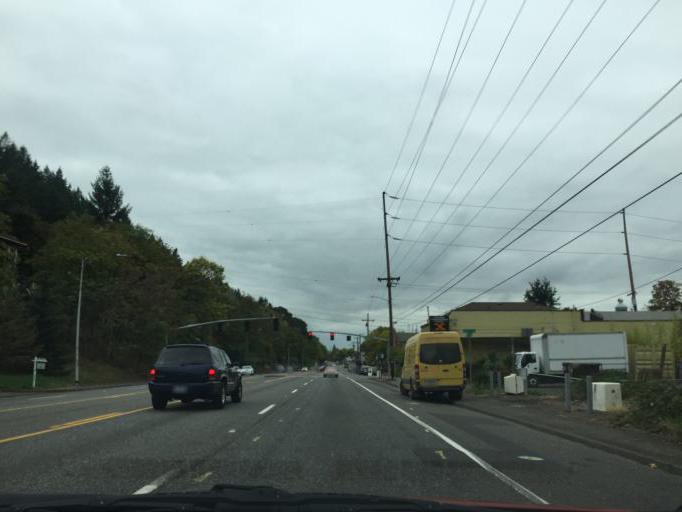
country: US
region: Oregon
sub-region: Washington County
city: Cedar Mill
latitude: 45.5980
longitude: -122.7853
